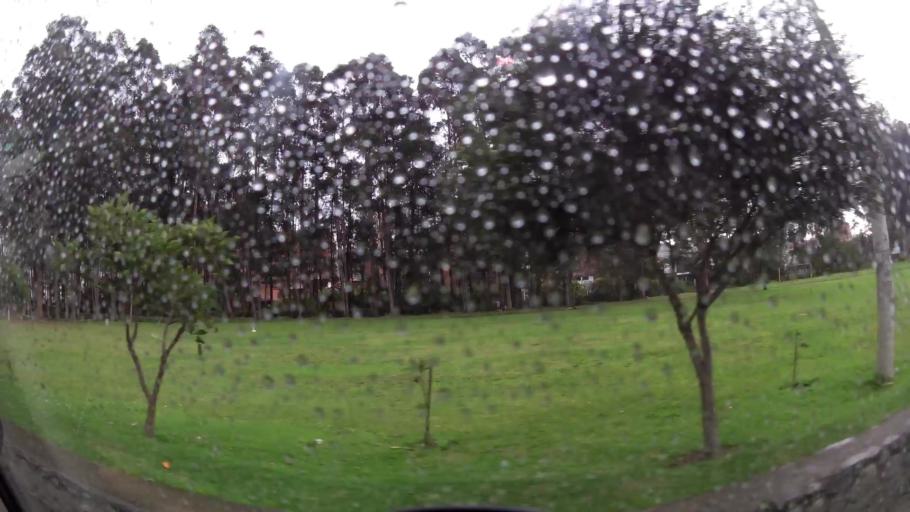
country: EC
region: Azuay
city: Cuenca
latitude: -2.8910
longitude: -79.0334
